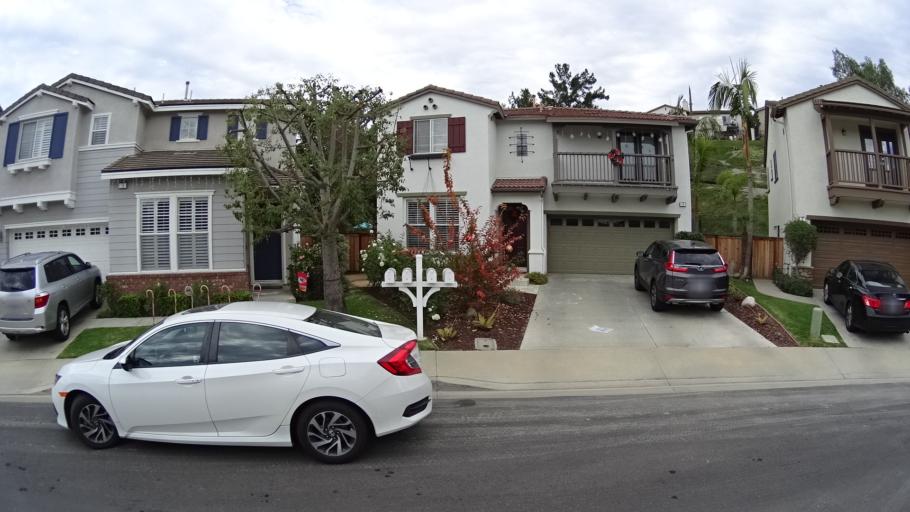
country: US
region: California
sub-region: Orange County
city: Aliso Viejo
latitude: 33.5638
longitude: -117.7419
